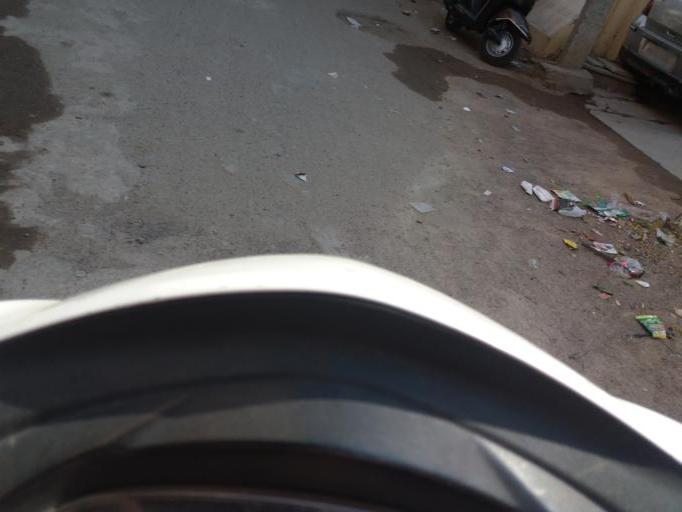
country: IN
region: Telangana
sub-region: Hyderabad
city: Malkajgiri
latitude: 17.4138
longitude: 78.5145
